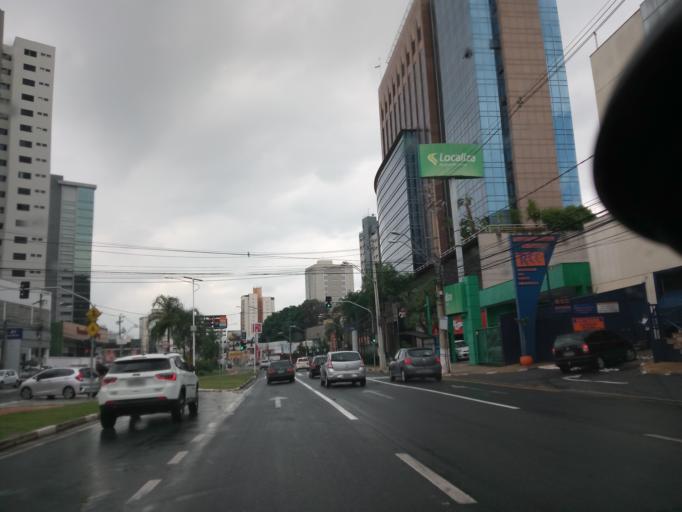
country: BR
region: Sao Paulo
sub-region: Campinas
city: Campinas
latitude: -22.8985
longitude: -47.0474
